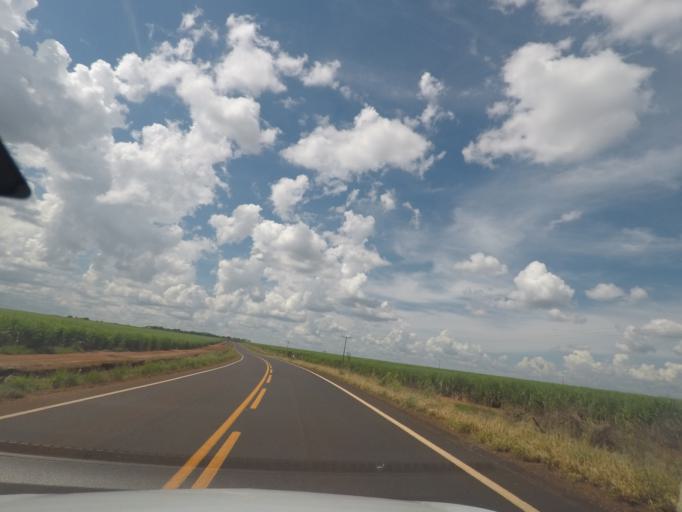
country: BR
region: Minas Gerais
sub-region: Conceicao Das Alagoas
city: Conceicao das Alagoas
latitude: -19.8601
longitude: -48.6011
